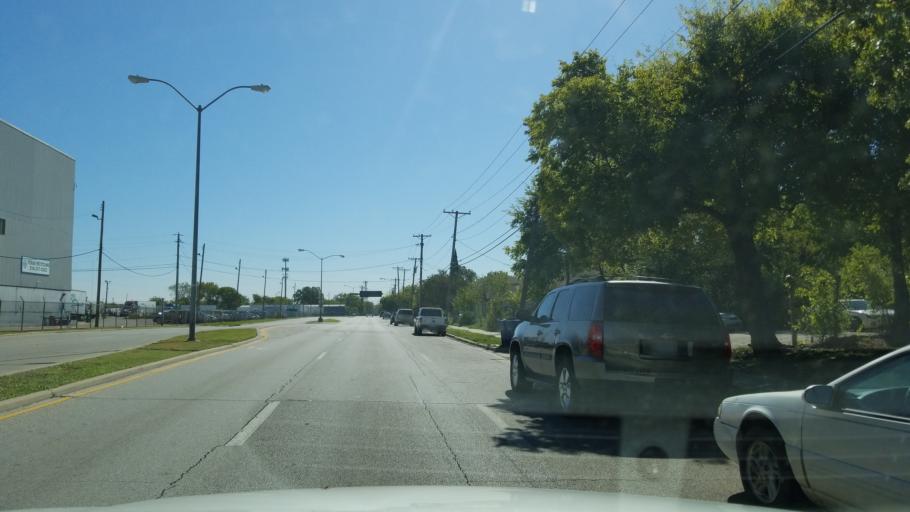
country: US
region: Texas
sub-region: Dallas County
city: Dallas
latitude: 32.7869
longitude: -96.7507
